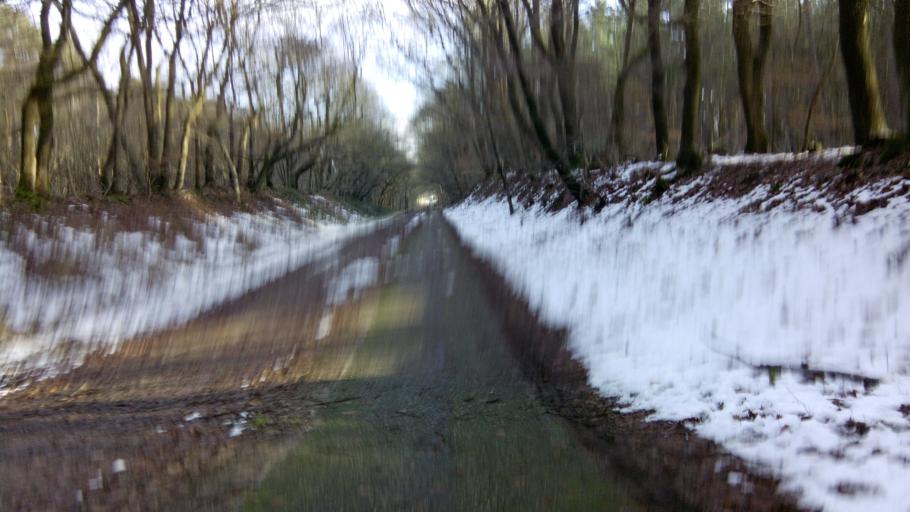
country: NL
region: Gelderland
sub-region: Gemeente Groesbeek
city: Groesbeek
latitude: 51.7873
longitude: 5.9082
